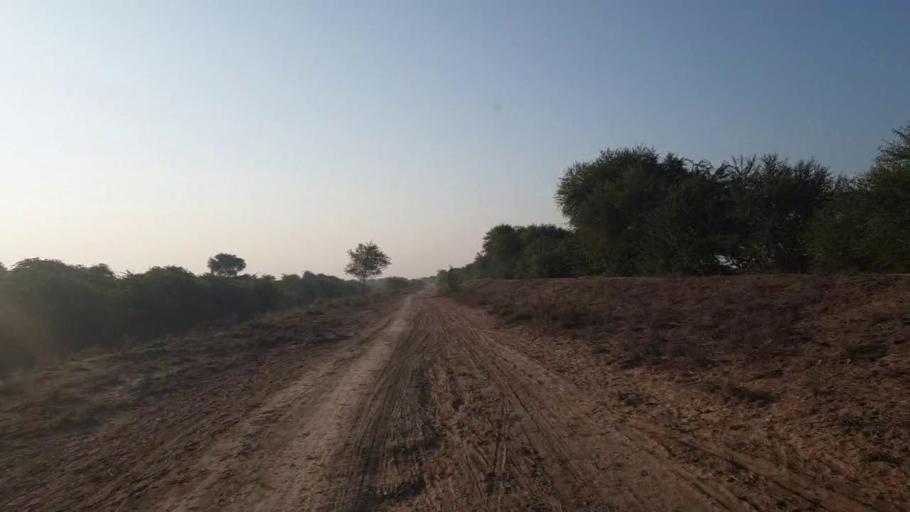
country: PK
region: Sindh
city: Badin
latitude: 24.6437
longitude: 68.7907
